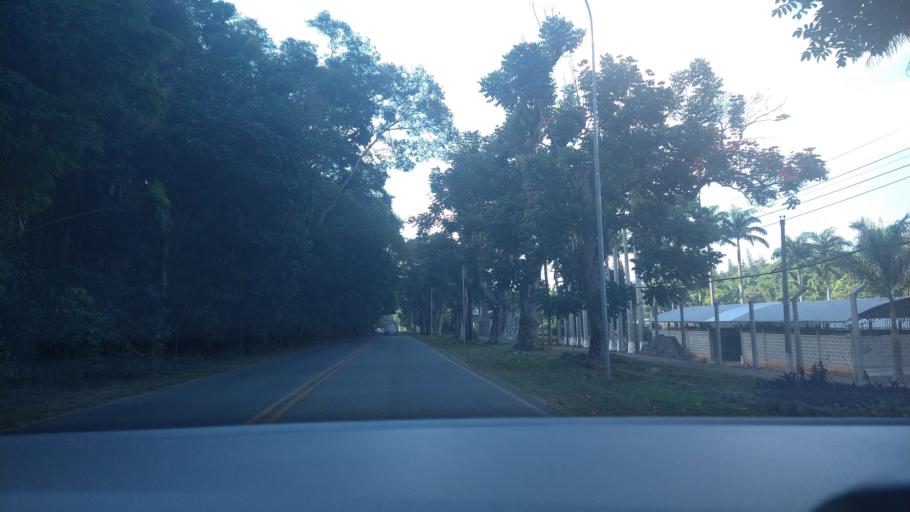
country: BR
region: Minas Gerais
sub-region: Vicosa
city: Vicosa
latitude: -20.7751
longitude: -42.8779
